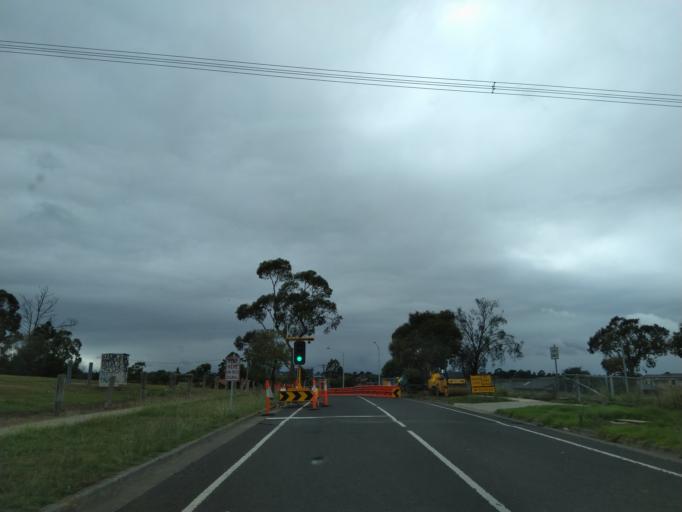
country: AU
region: Victoria
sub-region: Hume
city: Broadmeadows
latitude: -37.6706
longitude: 144.9047
